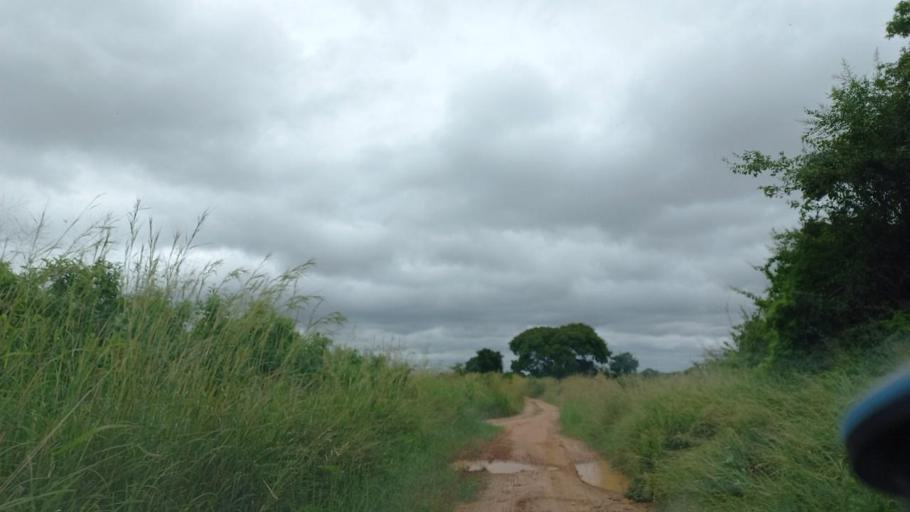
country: ZM
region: Lusaka
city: Lusaka
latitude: -15.1209
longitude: 28.3720
